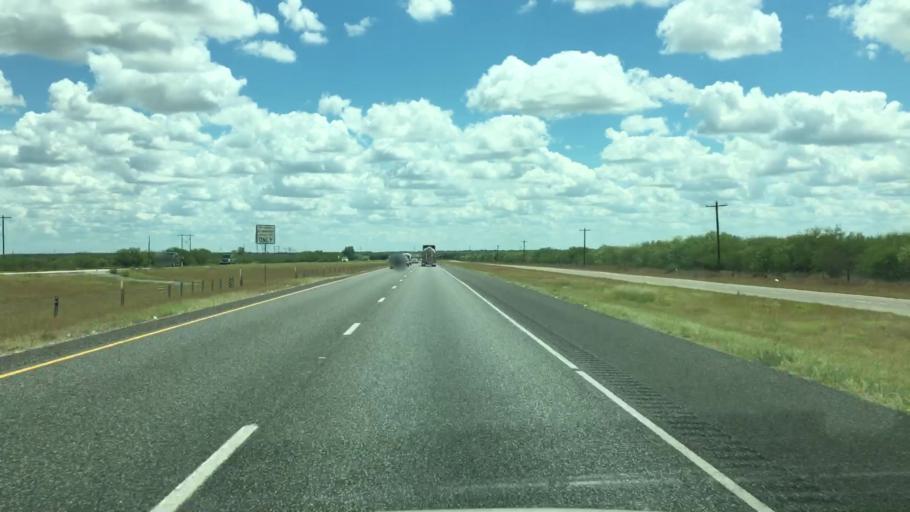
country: US
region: Texas
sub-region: Atascosa County
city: Pleasanton
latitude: 28.8594
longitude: -98.3869
